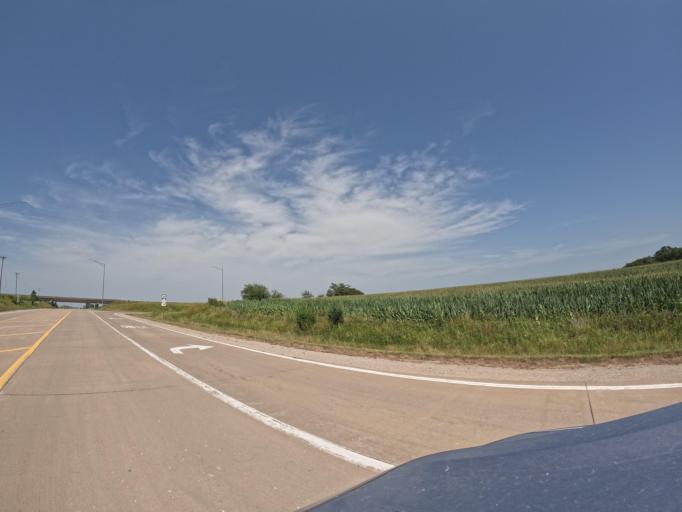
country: US
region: Iowa
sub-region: Henry County
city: Mount Pleasant
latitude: 40.9822
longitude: -91.6123
